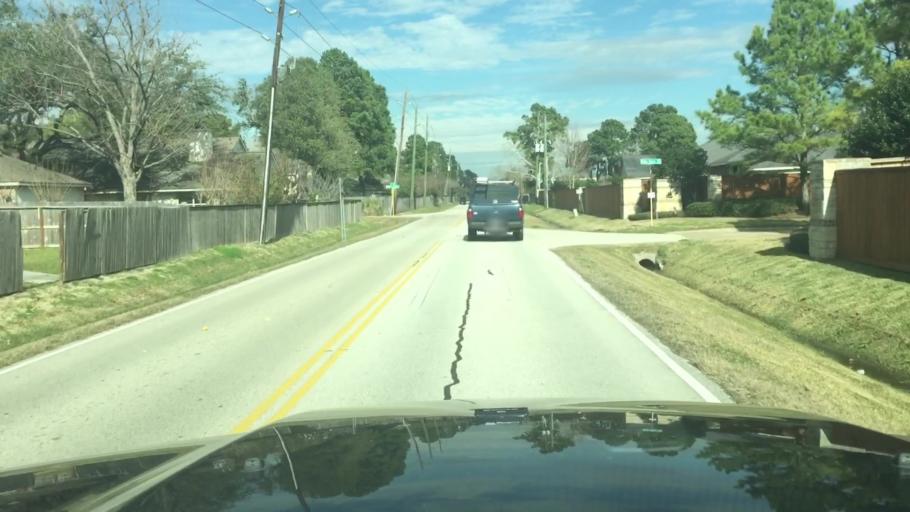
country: US
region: Texas
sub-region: Harris County
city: Oak Cliff Place
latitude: 29.8331
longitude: -95.6751
